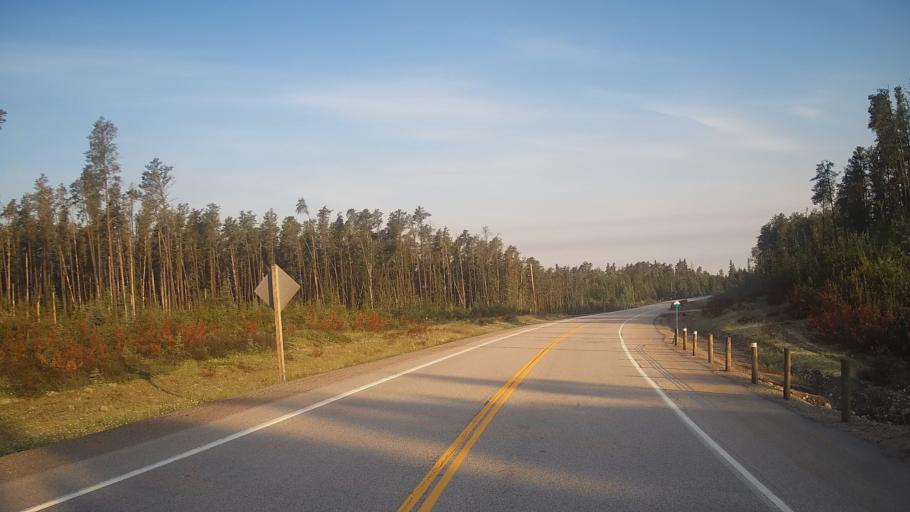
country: CA
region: Ontario
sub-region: Rainy River District
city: Atikokan
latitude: 49.2228
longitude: -90.9593
